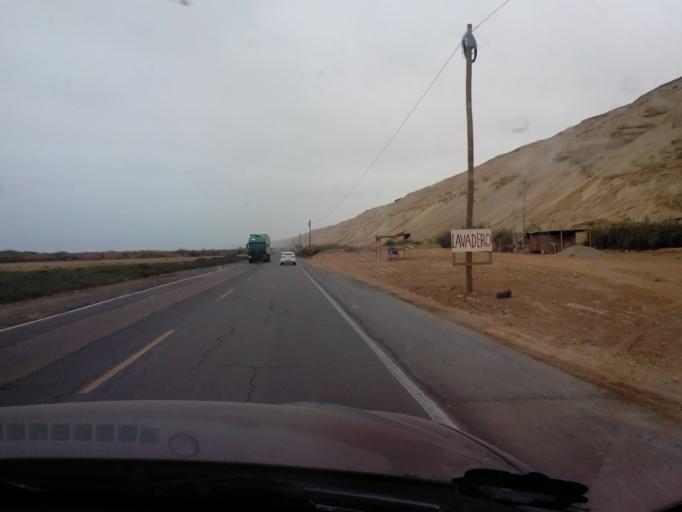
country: PE
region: Ica
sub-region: Provincia de Chincha
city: San Pedro
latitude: -13.4079
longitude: -76.1915
